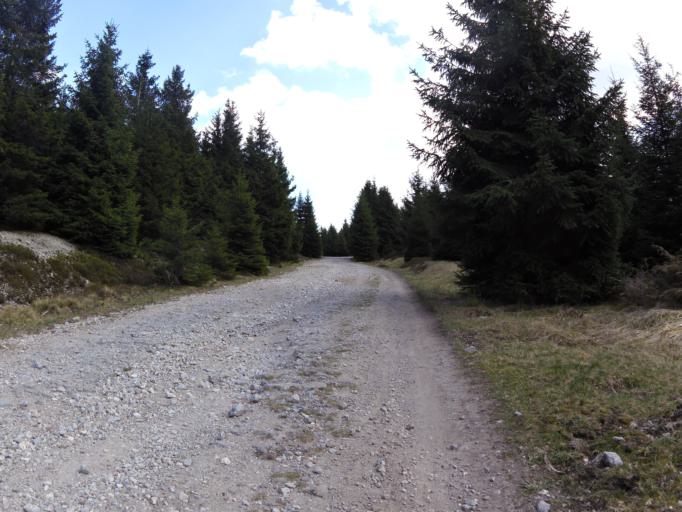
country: DE
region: Thuringia
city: Unterschonau
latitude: 50.7329
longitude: 10.6239
